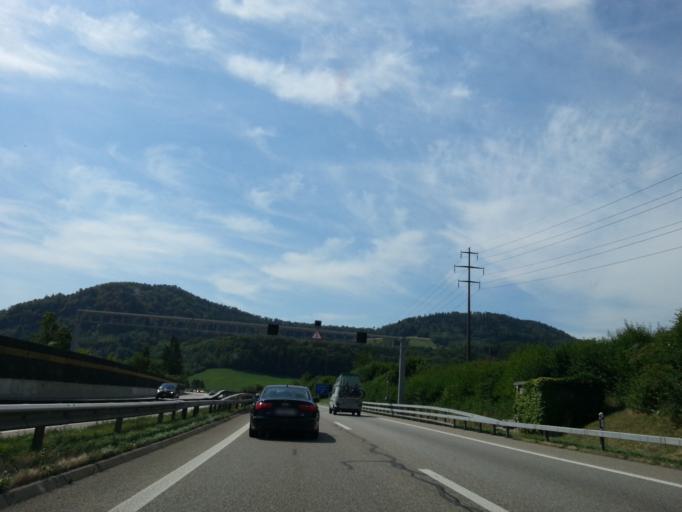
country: CH
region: Basel-Landschaft
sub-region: Bezirk Waldenburg
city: Diegten
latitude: 47.4076
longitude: 7.8068
